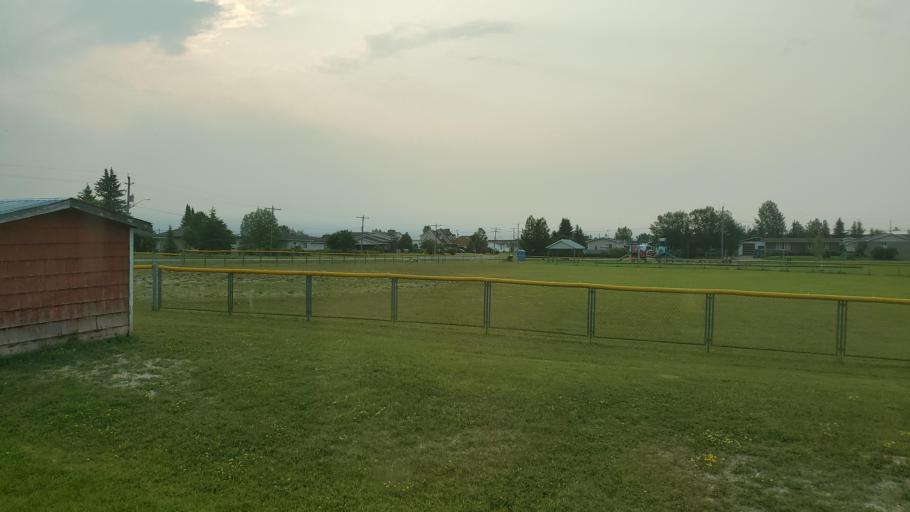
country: CA
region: Ontario
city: Hearst
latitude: 49.6102
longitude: -83.2668
